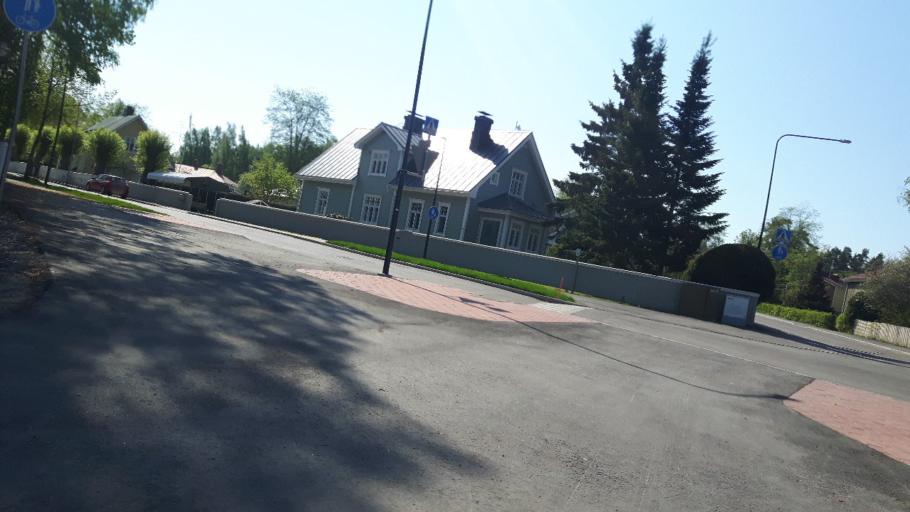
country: FI
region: Uusimaa
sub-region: Loviisa
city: Lovisa
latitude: 60.4475
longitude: 26.2362
